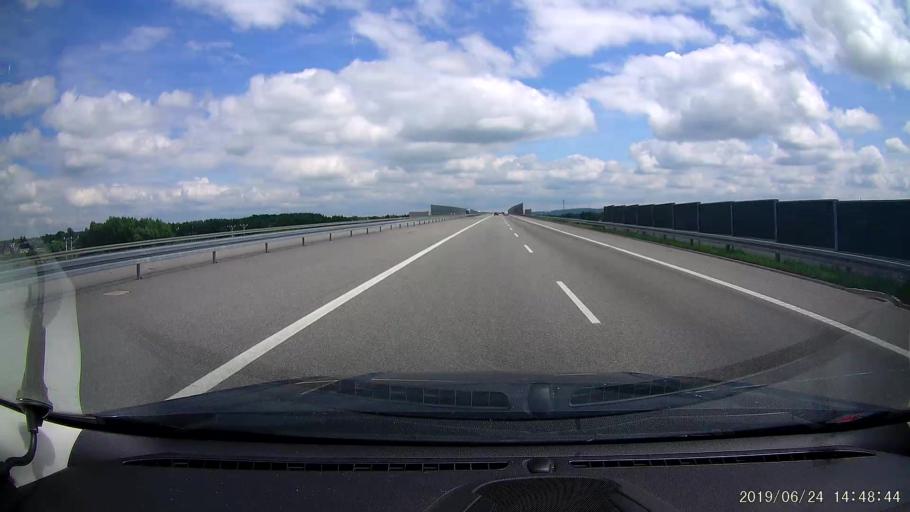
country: PL
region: Subcarpathian Voivodeship
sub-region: Powiat debicki
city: Brzeznica
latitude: 50.0850
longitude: 21.4482
